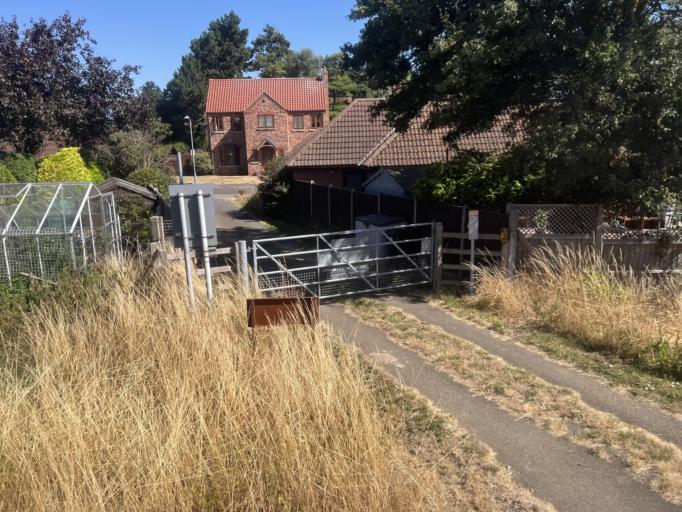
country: GB
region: England
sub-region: Lincolnshire
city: Heckington
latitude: 52.9788
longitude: -0.3036
